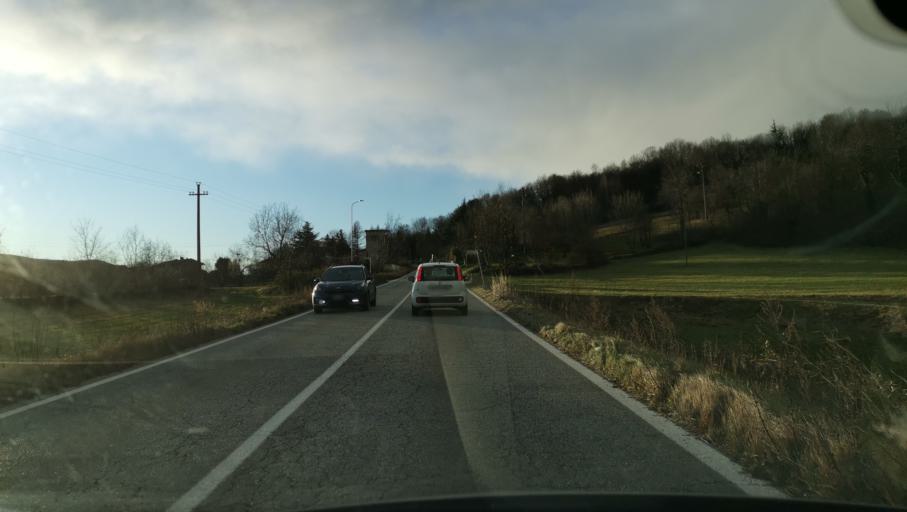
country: IT
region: Piedmont
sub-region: Provincia di Torino
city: Valgioie
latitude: 45.0550
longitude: 7.3732
